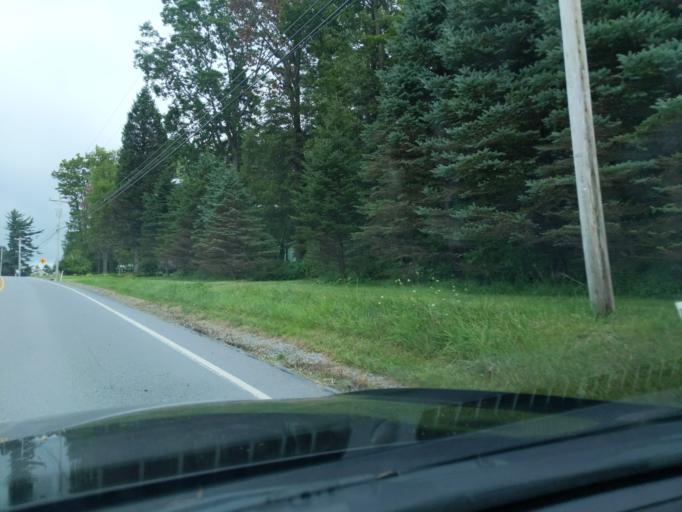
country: US
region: Pennsylvania
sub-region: Cambria County
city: Cresson
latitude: 40.3542
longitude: -78.5583
